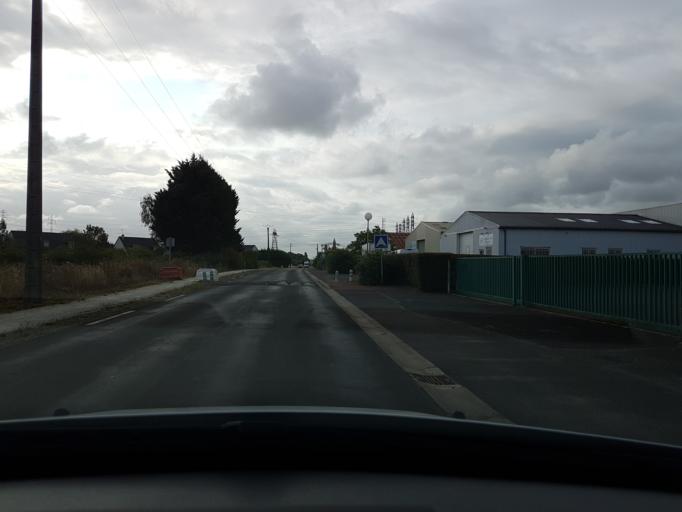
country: FR
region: Centre
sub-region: Departement d'Indre-et-Loire
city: Larcay
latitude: 47.3550
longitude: 0.7649
